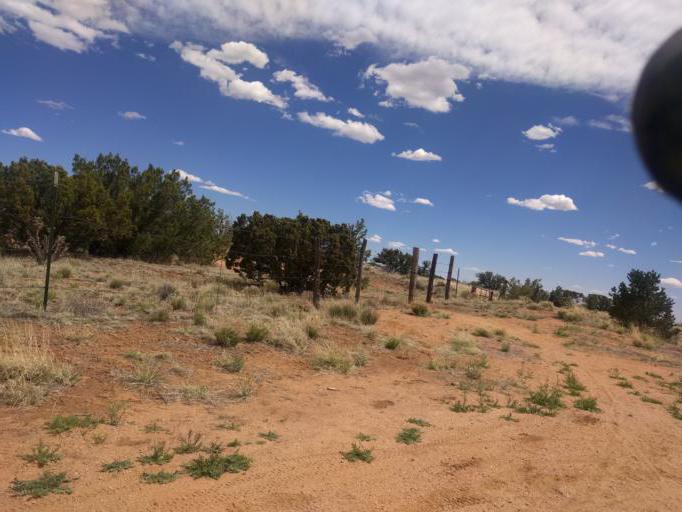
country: US
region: New Mexico
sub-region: Santa Fe County
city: Agua Fria
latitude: 35.6177
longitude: -105.9629
